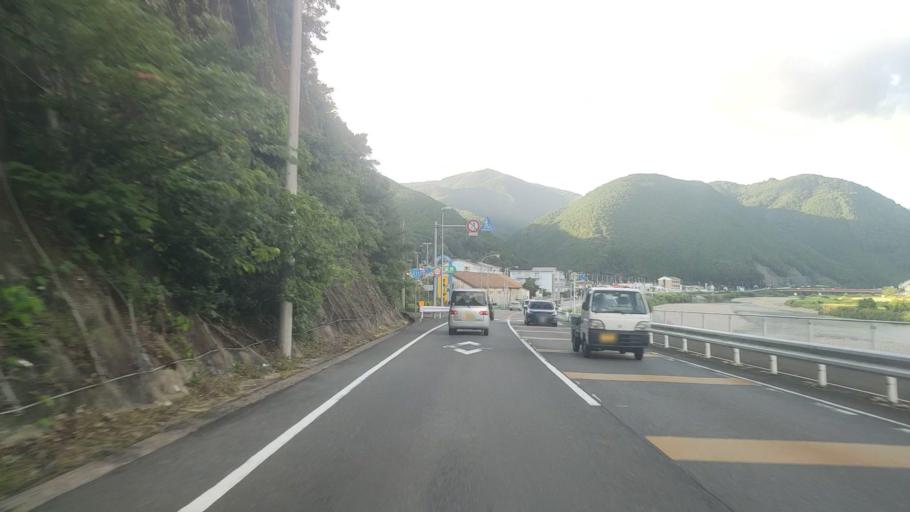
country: JP
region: Wakayama
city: Tanabe
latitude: 33.7238
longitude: 135.4812
